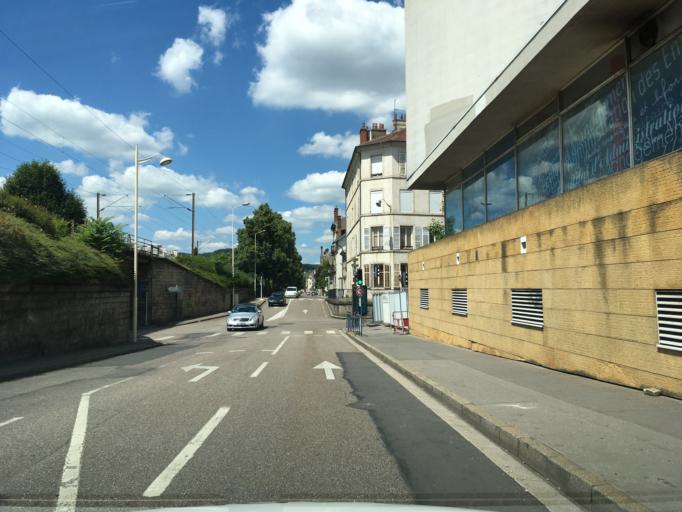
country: FR
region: Lorraine
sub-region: Departement de Meurthe-et-Moselle
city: Maxeville
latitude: 48.6969
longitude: 6.1706
